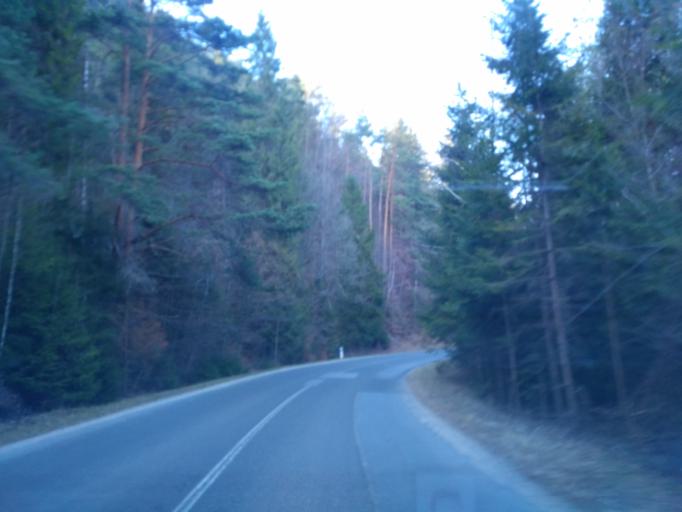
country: SK
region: Kosicky
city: Medzev
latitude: 48.7805
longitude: 20.7900
